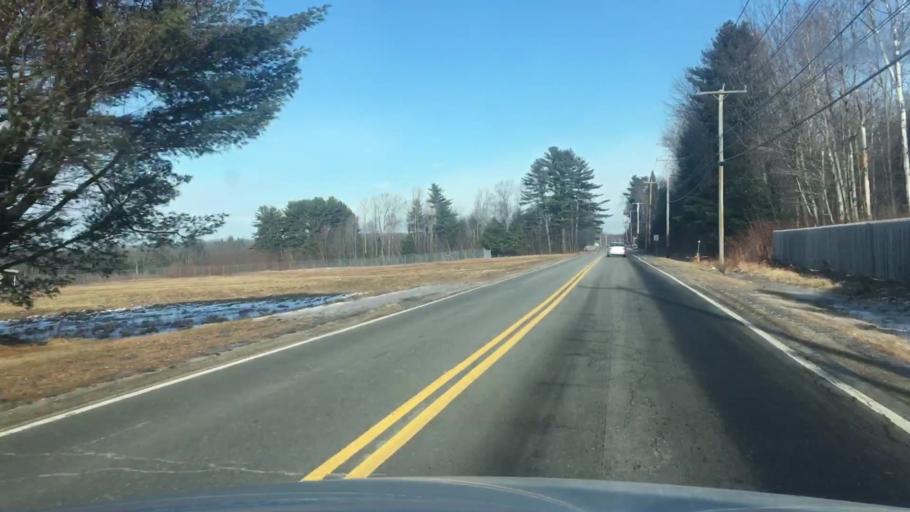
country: US
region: Maine
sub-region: Androscoggin County
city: Minot
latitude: 44.0533
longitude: -70.2758
